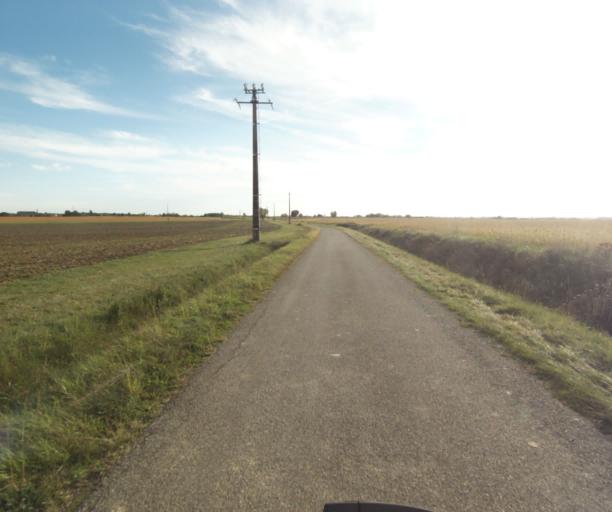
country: FR
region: Midi-Pyrenees
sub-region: Departement du Tarn-et-Garonne
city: Finhan
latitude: 43.9109
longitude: 1.1304
